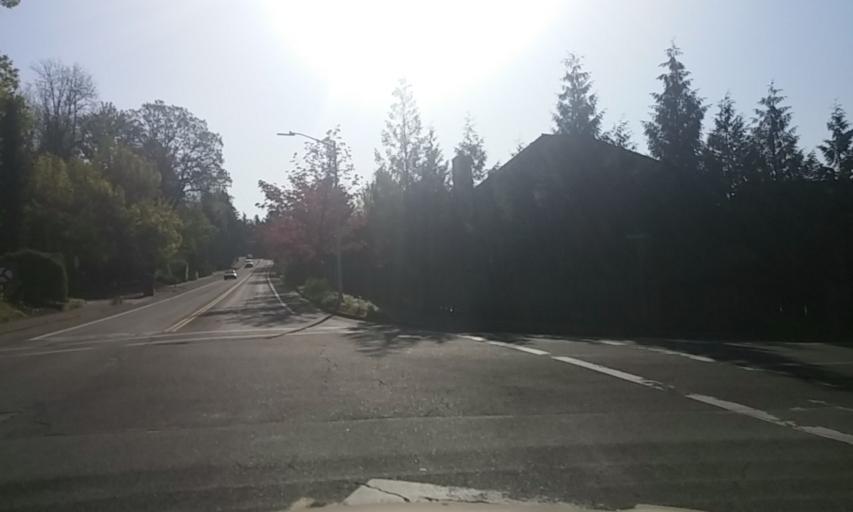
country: US
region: Oregon
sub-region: Washington County
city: Metzger
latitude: 45.4332
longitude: -122.7336
